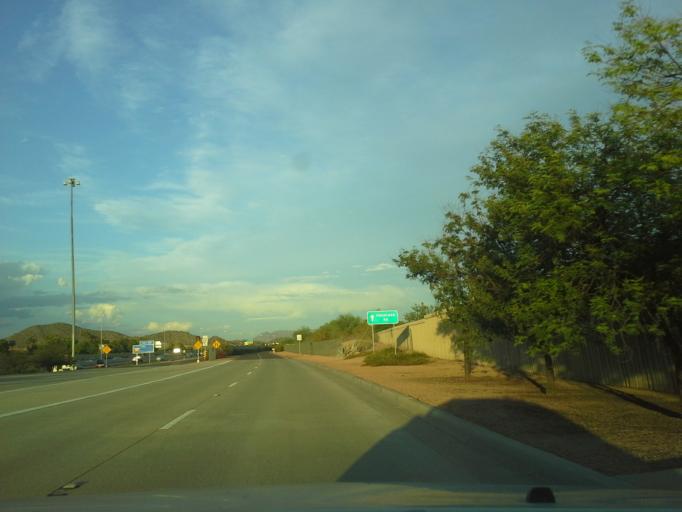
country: US
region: Arizona
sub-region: Maricopa County
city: Glendale
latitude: 33.6681
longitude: -112.0810
